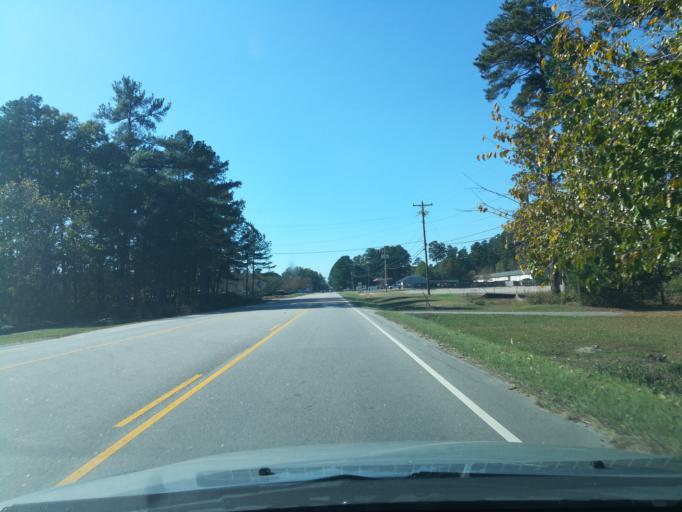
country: US
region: North Carolina
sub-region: Durham County
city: Durham
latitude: 36.0331
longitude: -78.9780
